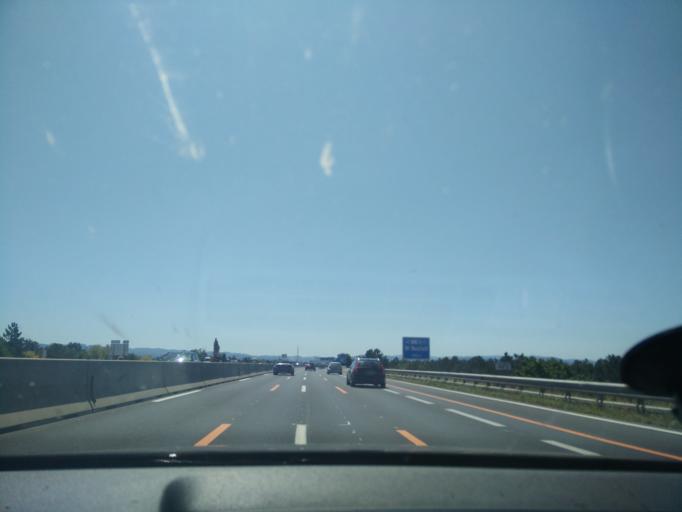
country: AT
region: Lower Austria
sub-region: Wiener Neustadt Stadt
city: Wiener Neustadt
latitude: 47.8033
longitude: 16.2001
